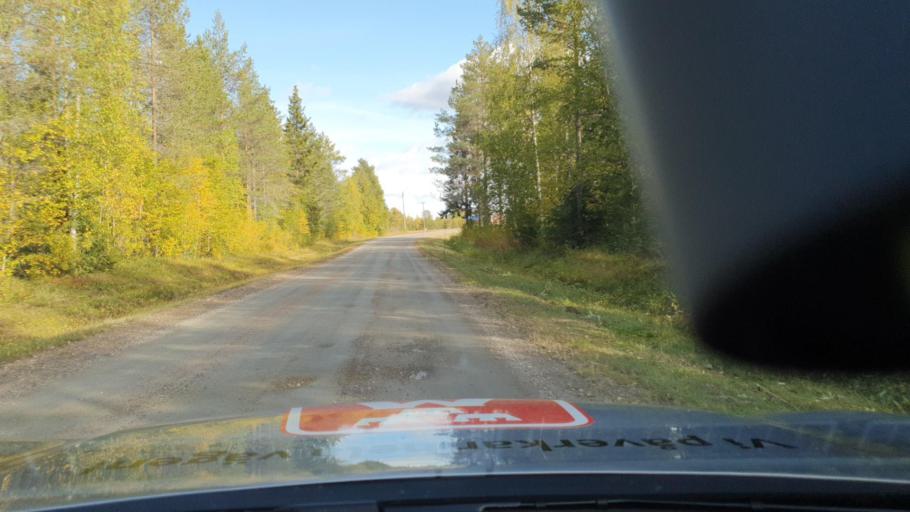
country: FI
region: Lapland
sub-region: Torniolaakso
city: Ylitornio
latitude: 65.9629
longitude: 23.6718
